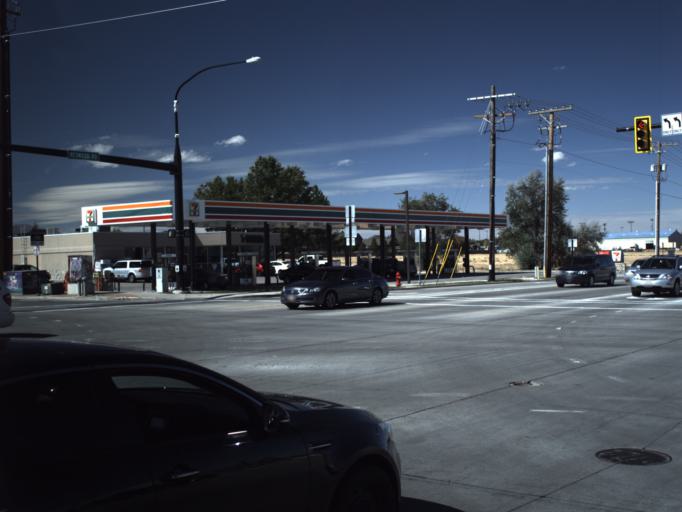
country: US
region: Utah
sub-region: Salt Lake County
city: South Jordan
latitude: 40.5441
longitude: -111.9386
